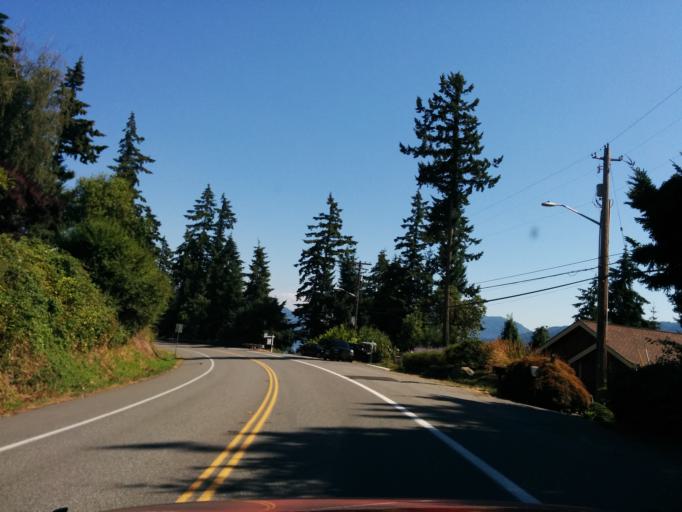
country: US
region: Washington
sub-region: King County
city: West Lake Sammamish
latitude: 47.5831
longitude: -122.0823
